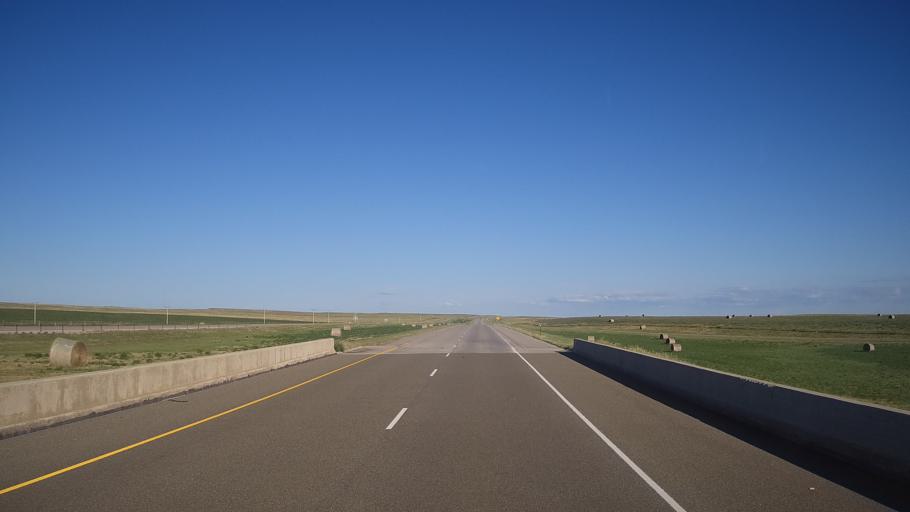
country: US
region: South Dakota
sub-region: Haakon County
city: Philip
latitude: 43.8675
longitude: -101.9600
